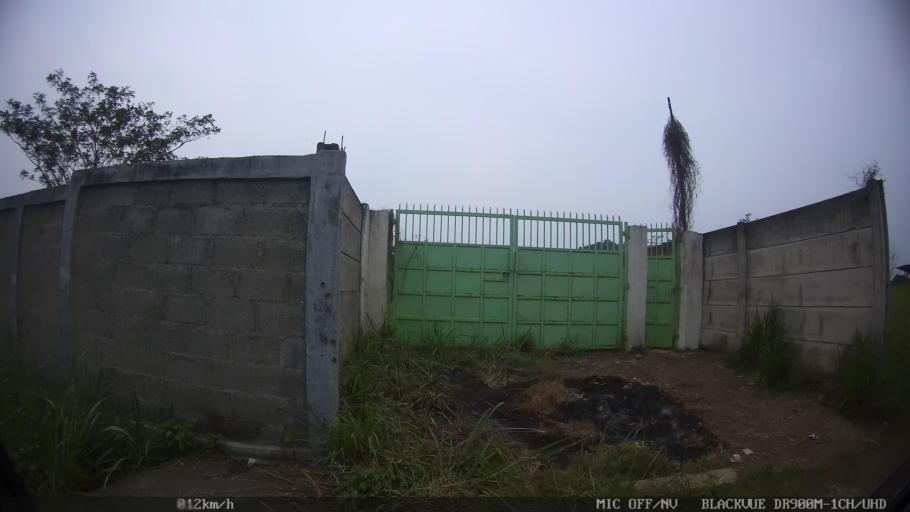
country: ID
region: Lampung
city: Panjang
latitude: -5.4220
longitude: 105.3487
